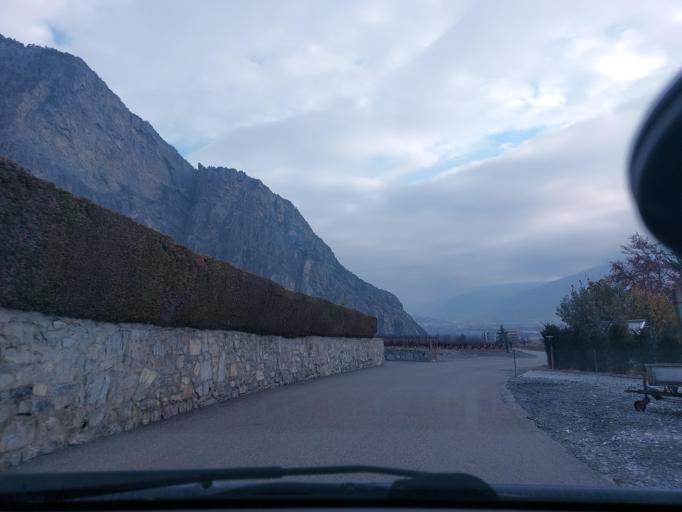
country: CH
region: Valais
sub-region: Conthey District
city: Chamoson
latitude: 46.2019
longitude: 7.2284
